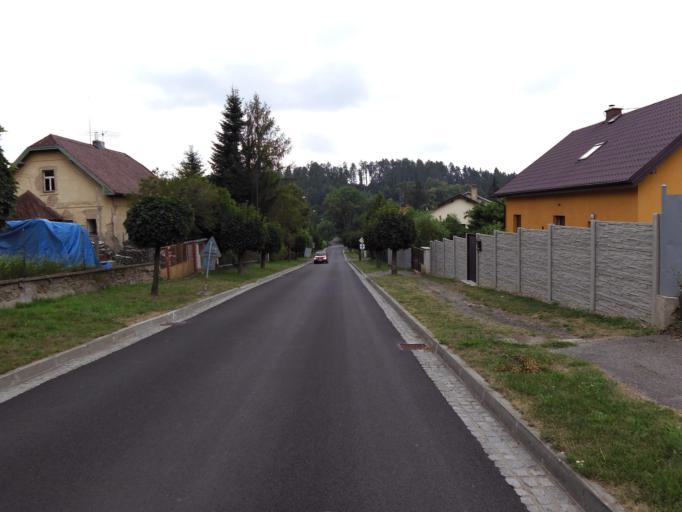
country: CZ
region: Central Bohemia
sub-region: Okres Benesov
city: Pysely
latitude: 49.8740
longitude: 14.6794
